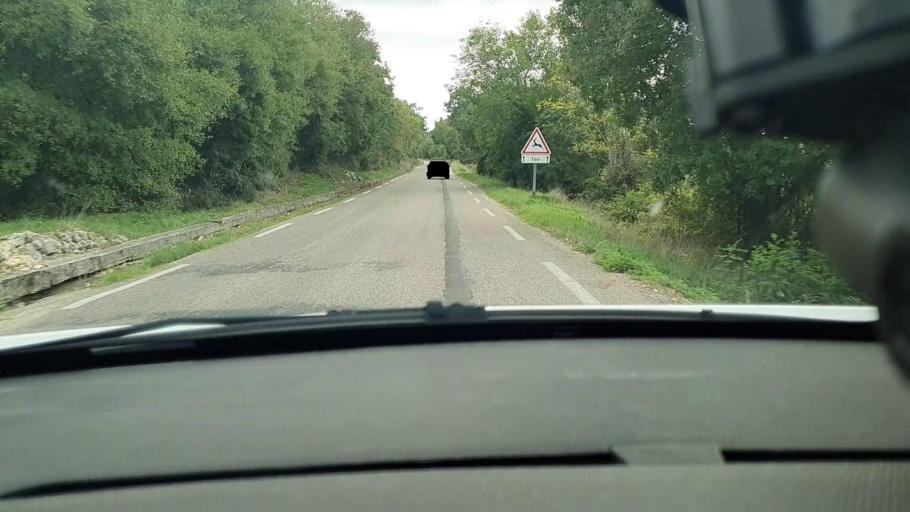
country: FR
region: Languedoc-Roussillon
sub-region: Departement du Gard
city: Salindres
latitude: 44.1753
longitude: 4.2387
